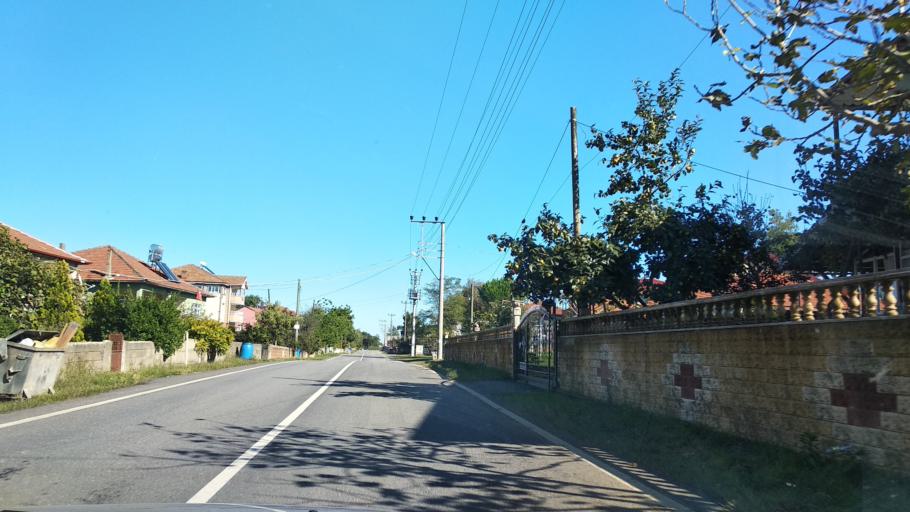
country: TR
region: Sakarya
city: Karasu
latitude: 41.1180
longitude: 30.6220
